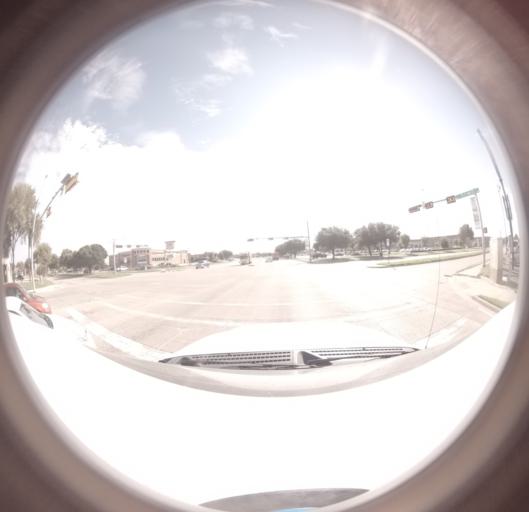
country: US
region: Texas
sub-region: Ector County
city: West Odessa
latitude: 31.7423
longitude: -102.5314
